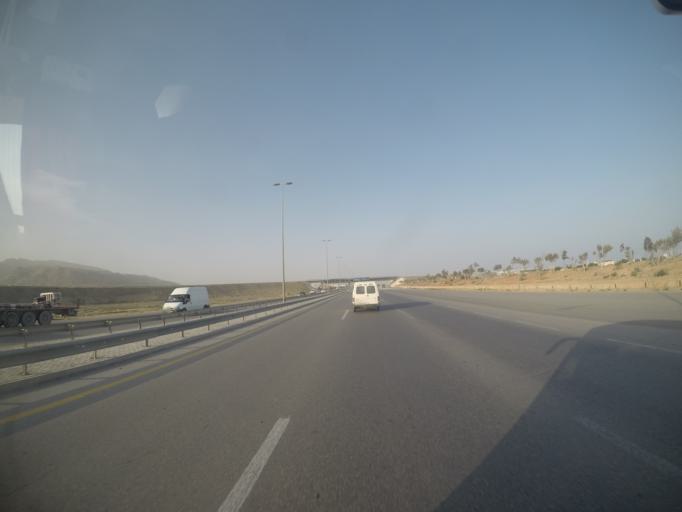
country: AZ
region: Baki
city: Korgoz
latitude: 40.2544
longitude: 49.6271
